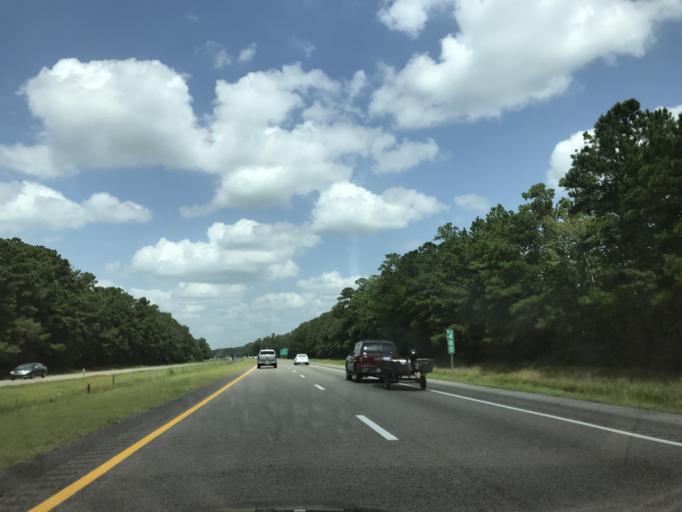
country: US
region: North Carolina
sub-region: Pender County
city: Burgaw
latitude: 34.5534
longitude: -77.8939
